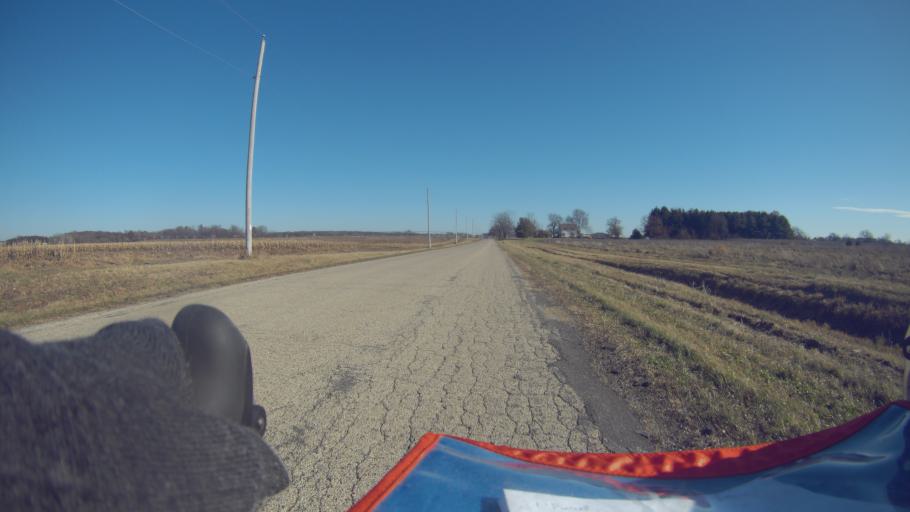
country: US
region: Wisconsin
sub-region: Green County
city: Brooklyn
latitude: 42.8710
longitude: -89.4031
